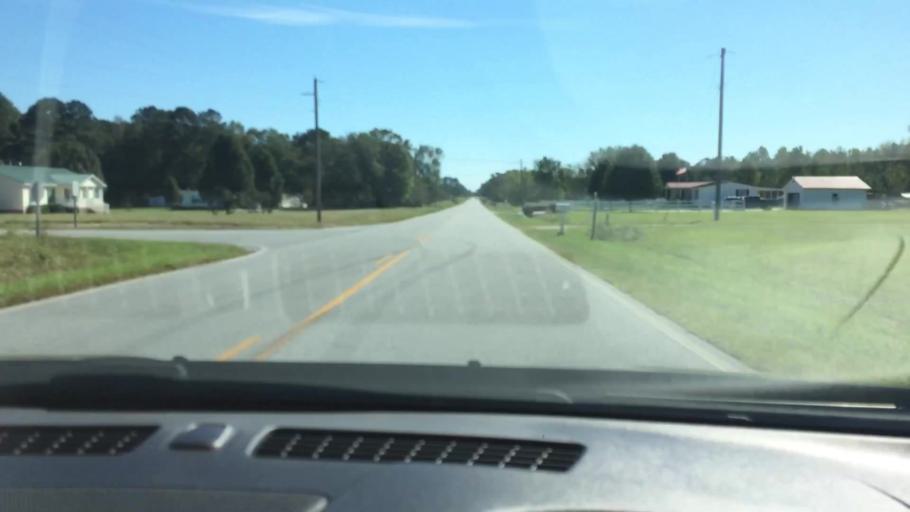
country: US
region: North Carolina
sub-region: Pitt County
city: Grifton
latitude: 35.3932
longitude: -77.3920
